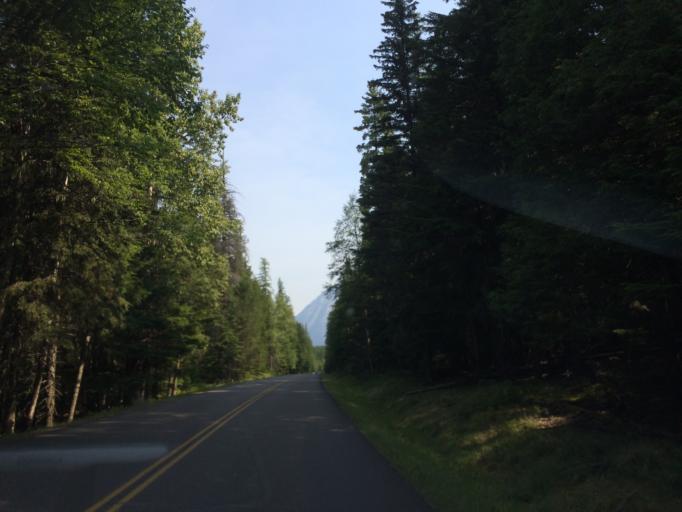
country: US
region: Montana
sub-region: Flathead County
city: Columbia Falls
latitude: 48.6227
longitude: -113.8707
